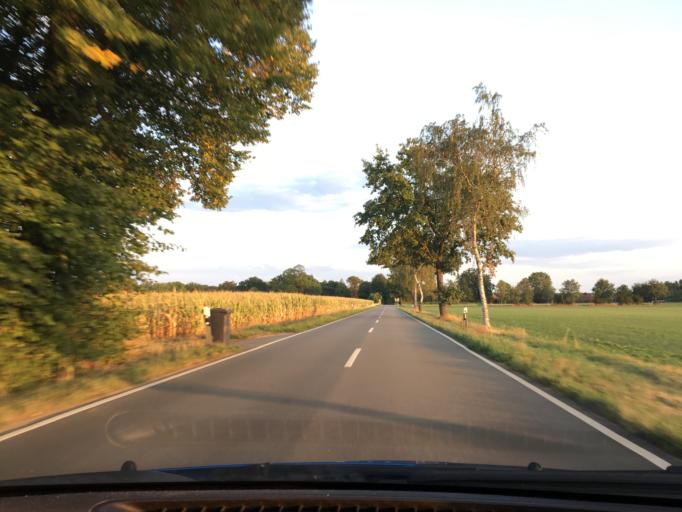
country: DE
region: Lower Saxony
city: Tosterglope
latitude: 53.2138
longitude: 10.8167
